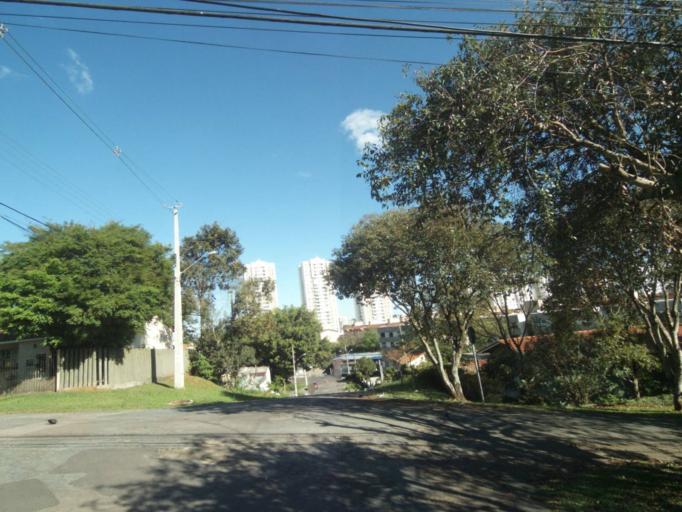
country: BR
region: Parana
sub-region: Curitiba
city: Curitiba
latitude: -25.3856
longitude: -49.2380
